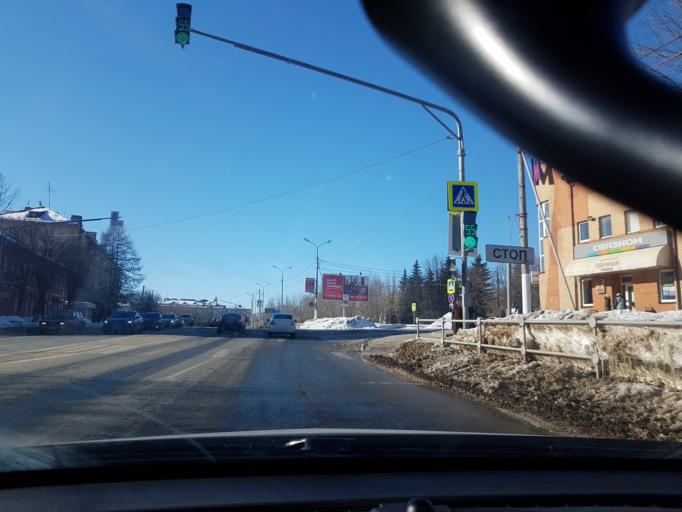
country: RU
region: Moskovskaya
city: Istra
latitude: 55.9137
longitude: 36.8624
